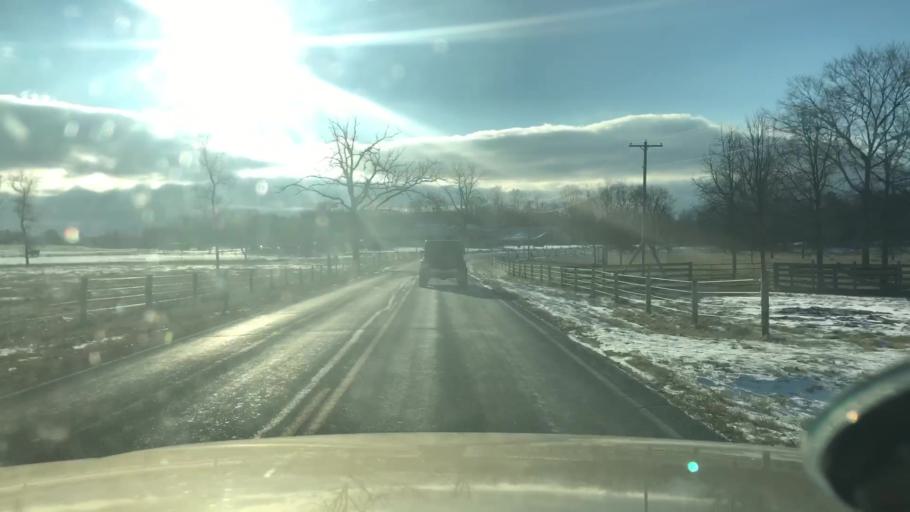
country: US
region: Michigan
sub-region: Jackson County
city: Vandercook Lake
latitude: 42.0946
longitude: -84.4620
